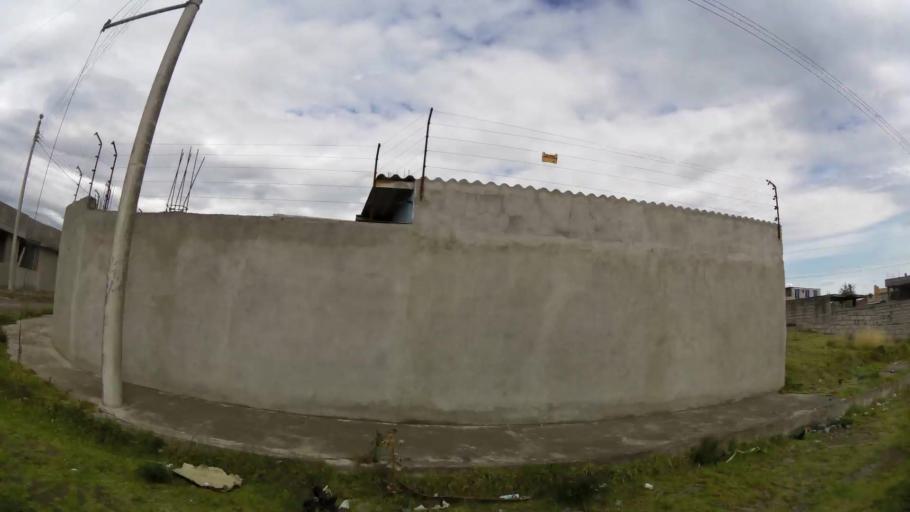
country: EC
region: Cotopaxi
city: Latacunga
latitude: -0.9487
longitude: -78.6173
